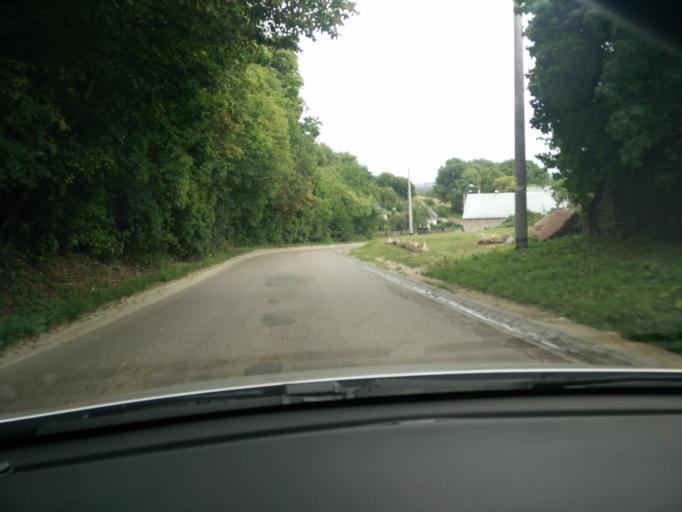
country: PL
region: Pomeranian Voivodeship
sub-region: Powiat pucki
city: Mrzezino
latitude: 54.6520
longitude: 18.4306
